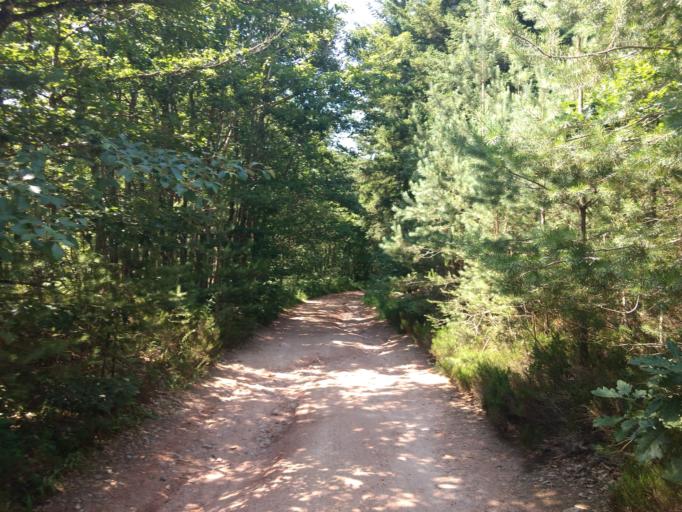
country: FR
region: Midi-Pyrenees
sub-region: Departement de l'Aveyron
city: Laissac
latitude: 44.3661
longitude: 2.7549
